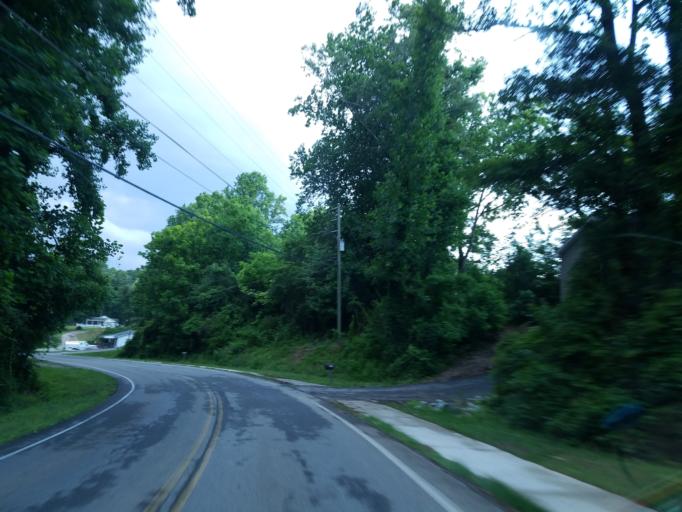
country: US
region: Georgia
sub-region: Lumpkin County
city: Dahlonega
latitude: 34.5366
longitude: -83.9834
